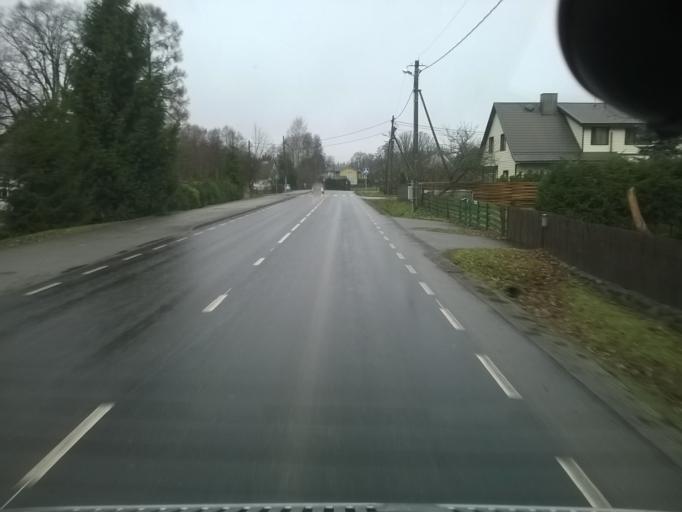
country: EE
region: Harju
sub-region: Saku vald
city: Saku
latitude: 59.2383
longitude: 24.6815
